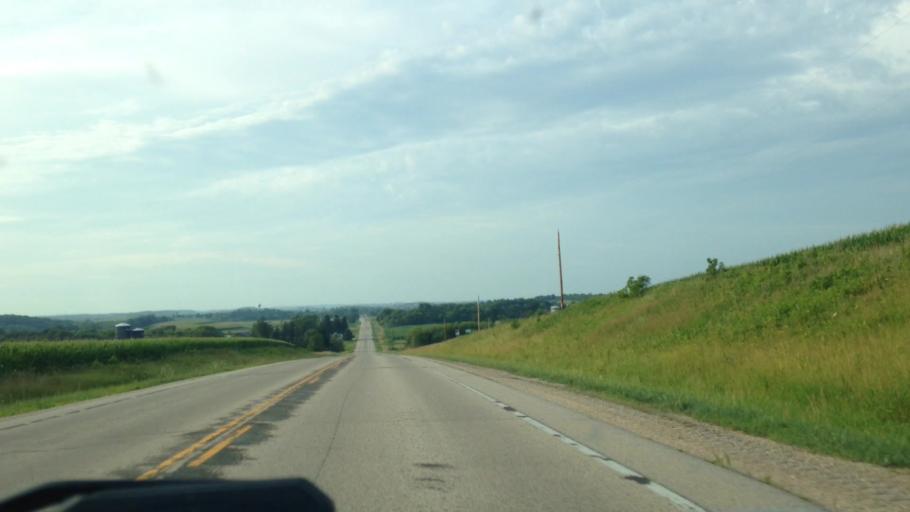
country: US
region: Wisconsin
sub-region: Dodge County
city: Theresa
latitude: 43.4827
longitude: -88.4501
